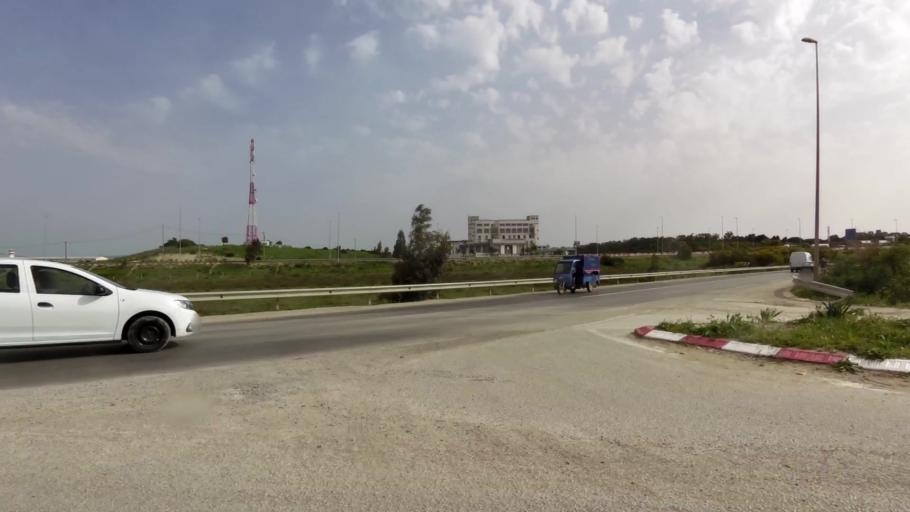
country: MA
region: Tanger-Tetouan
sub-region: Tanger-Assilah
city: Boukhalef
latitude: 35.6815
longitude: -5.9243
